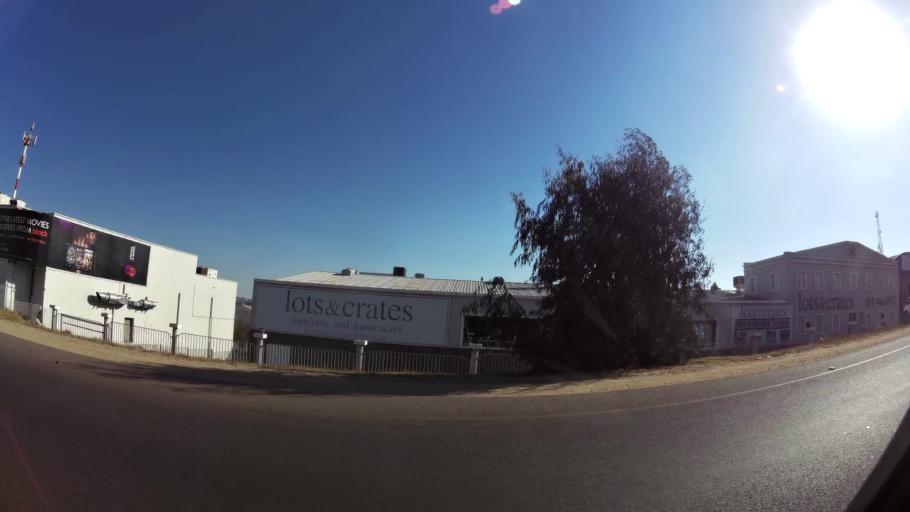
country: ZA
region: Gauteng
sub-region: City of Johannesburg Metropolitan Municipality
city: Midrand
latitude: -26.0009
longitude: 28.0758
